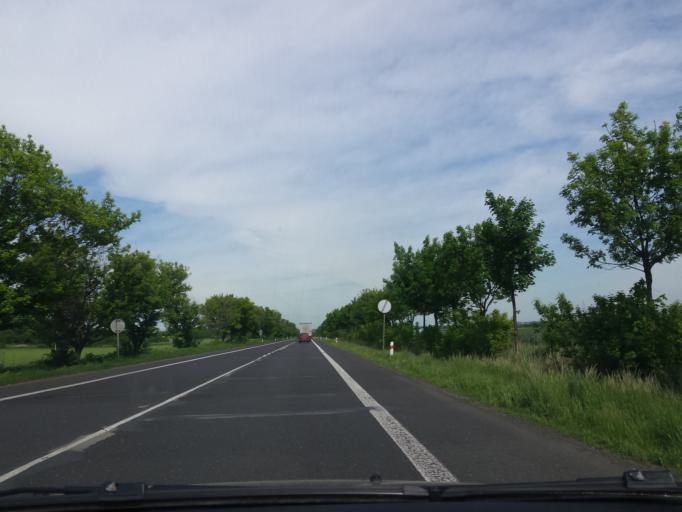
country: CZ
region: Central Bohemia
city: Luzec nad Vltavou
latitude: 50.3420
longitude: 14.3997
